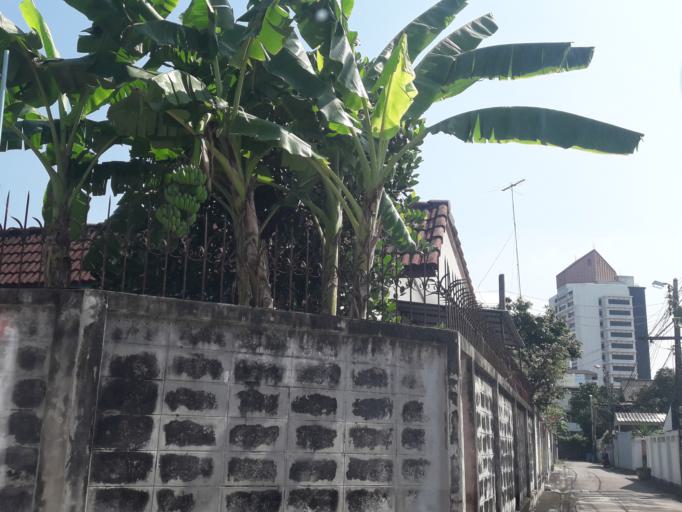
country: TH
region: Bangkok
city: Bangkok Yai
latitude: 13.7390
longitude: 100.4688
